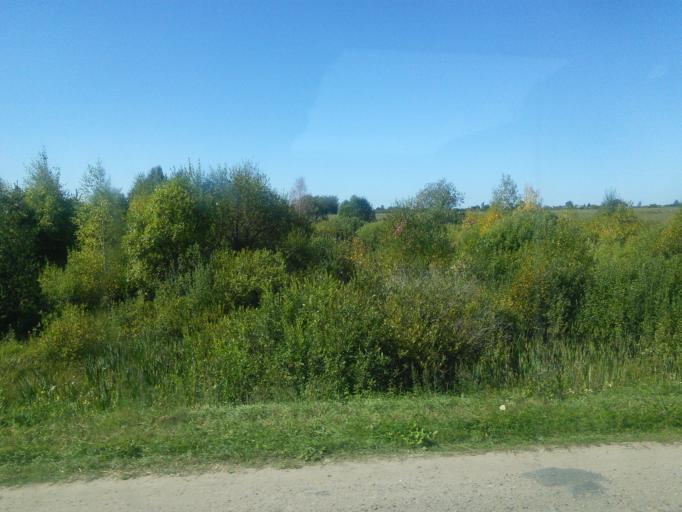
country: RU
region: Tverskaya
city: Kalyazin
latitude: 57.2143
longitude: 37.8690
